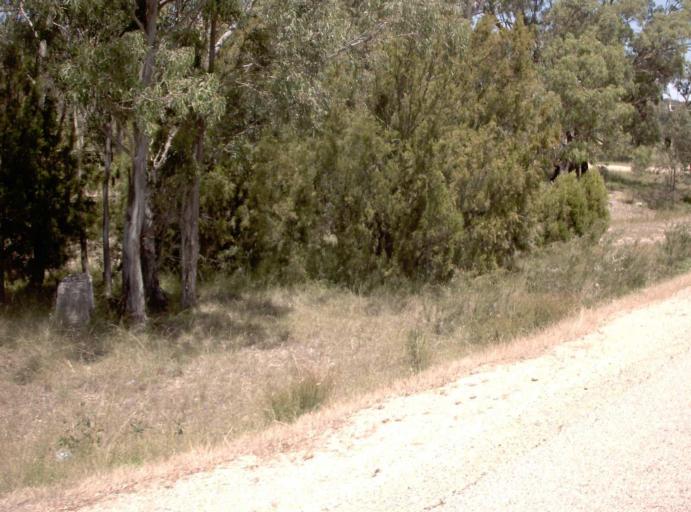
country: AU
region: Victoria
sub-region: East Gippsland
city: Bairnsdale
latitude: -37.7631
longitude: 147.7008
